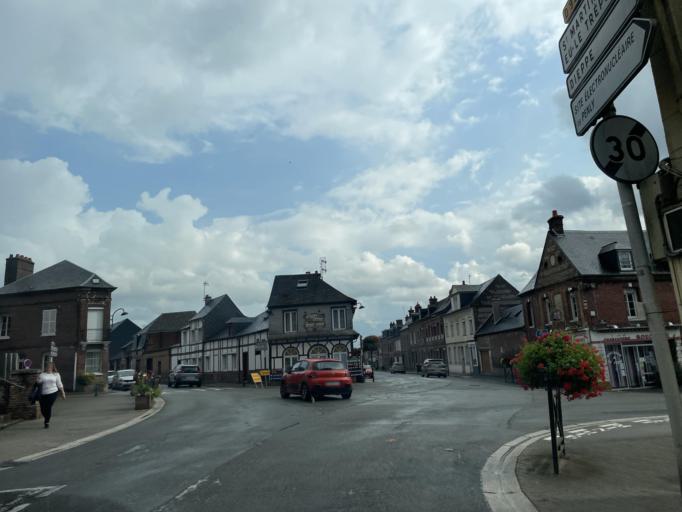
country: FR
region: Haute-Normandie
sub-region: Departement de la Seine-Maritime
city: Envermeu
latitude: 49.8957
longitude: 1.2649
